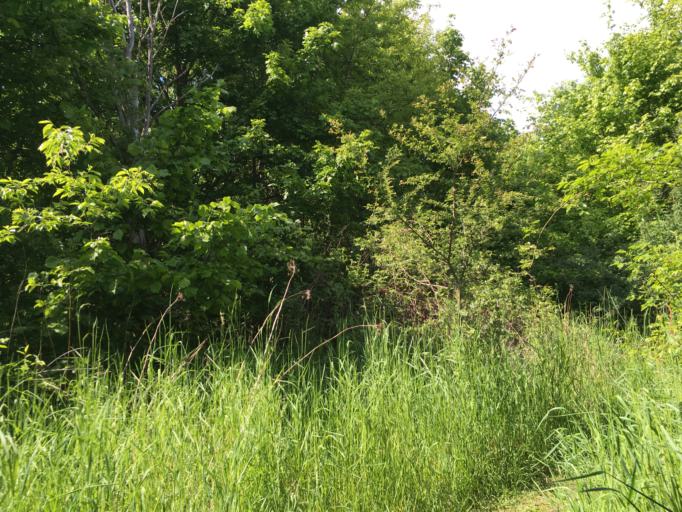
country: DE
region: Berlin
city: Wartenberg
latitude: 52.5771
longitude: 13.4977
